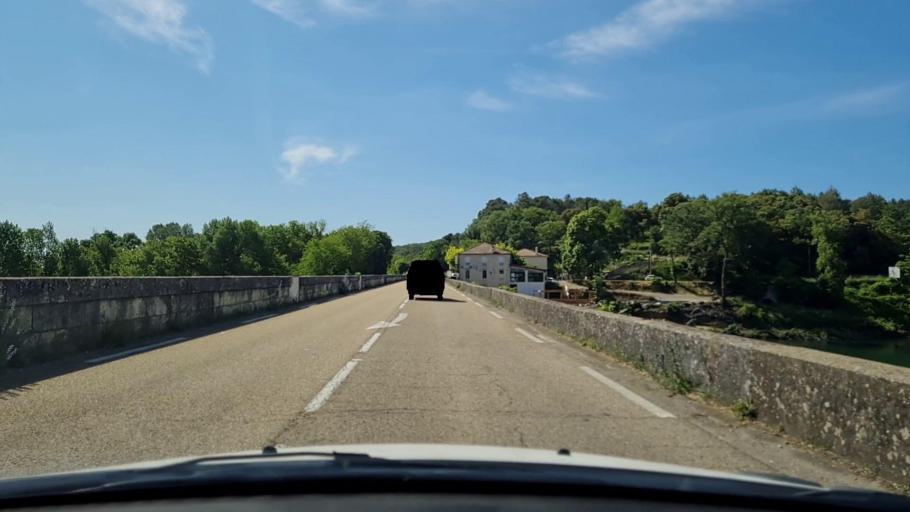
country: FR
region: Languedoc-Roussillon
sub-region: Departement du Gard
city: Vezenobres
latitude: 44.0182
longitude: 4.1563
